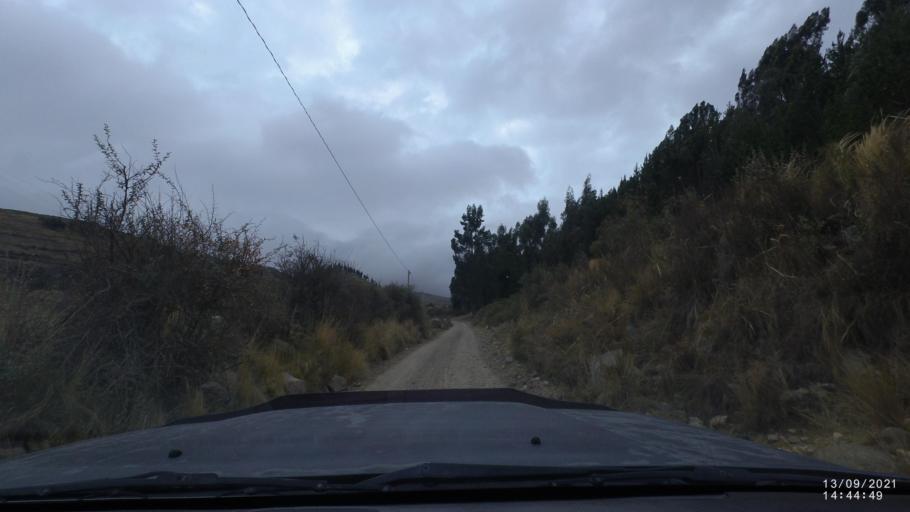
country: BO
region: Cochabamba
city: Colomi
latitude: -17.3562
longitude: -65.8105
